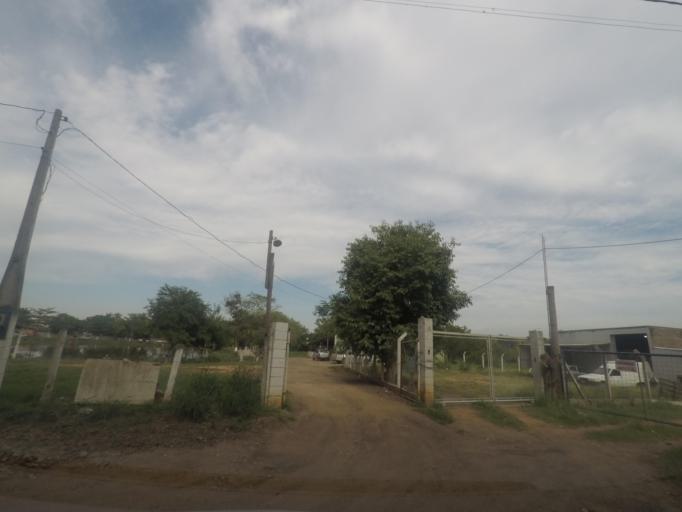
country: BR
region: Sao Paulo
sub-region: Sumare
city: Sumare
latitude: -22.7960
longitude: -47.2525
